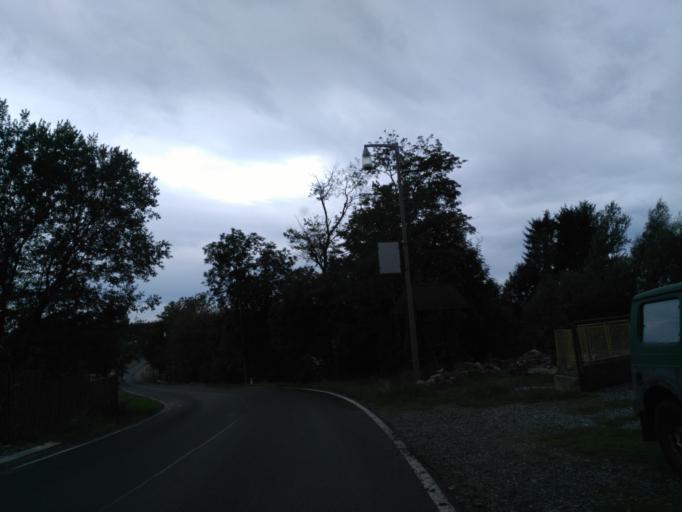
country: CZ
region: Karlovarsky
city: Abertamy
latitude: 50.3673
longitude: 12.8117
